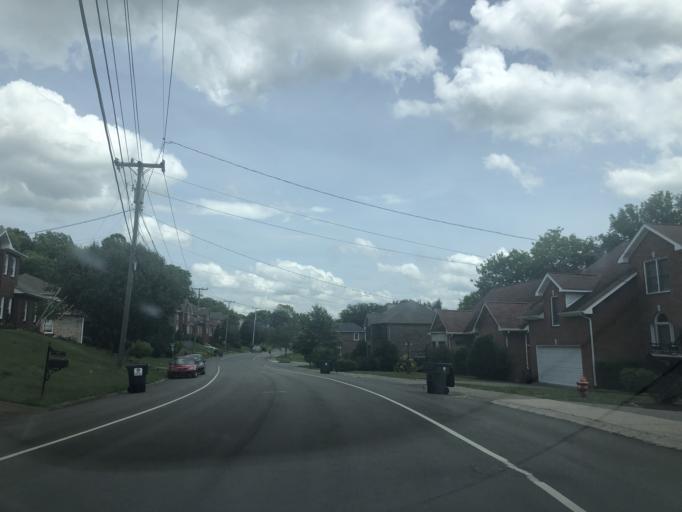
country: US
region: Tennessee
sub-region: Cheatham County
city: Pegram
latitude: 36.0522
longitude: -86.9605
